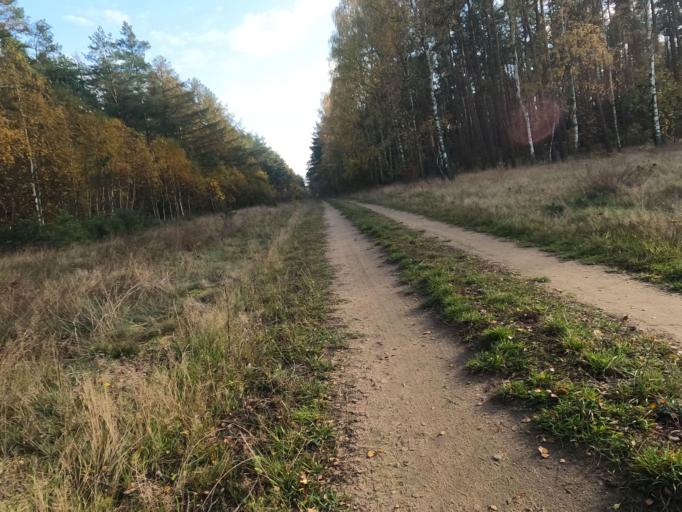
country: PL
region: West Pomeranian Voivodeship
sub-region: Powiat szczecinecki
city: Lubowo
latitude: 53.5789
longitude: 16.4010
